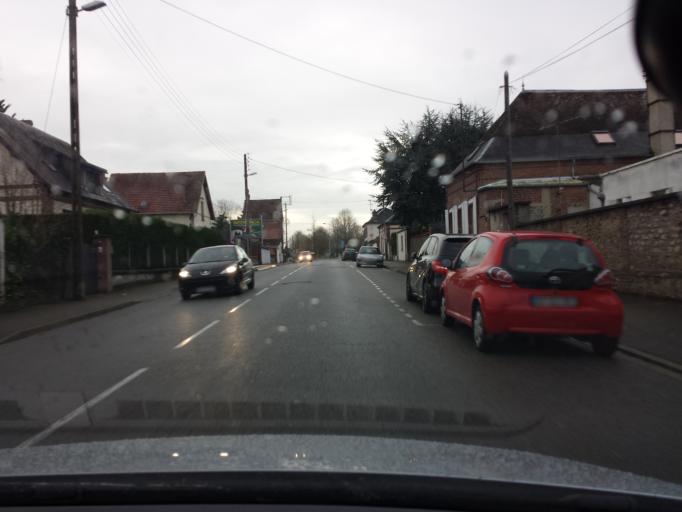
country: FR
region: Haute-Normandie
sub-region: Departement de l'Eure
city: Evreux
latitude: 49.0085
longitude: 1.1516
